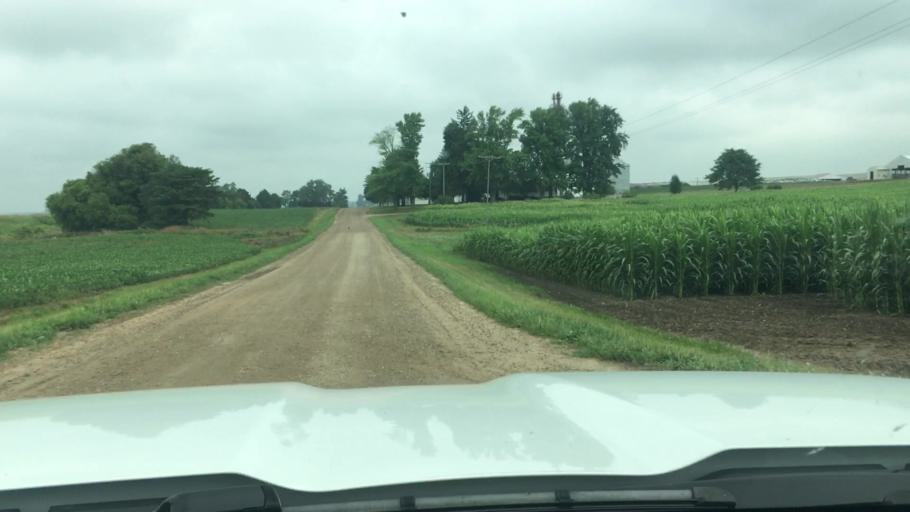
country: US
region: Michigan
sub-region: Sanilac County
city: Marlette
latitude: 43.3447
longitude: -82.9752
